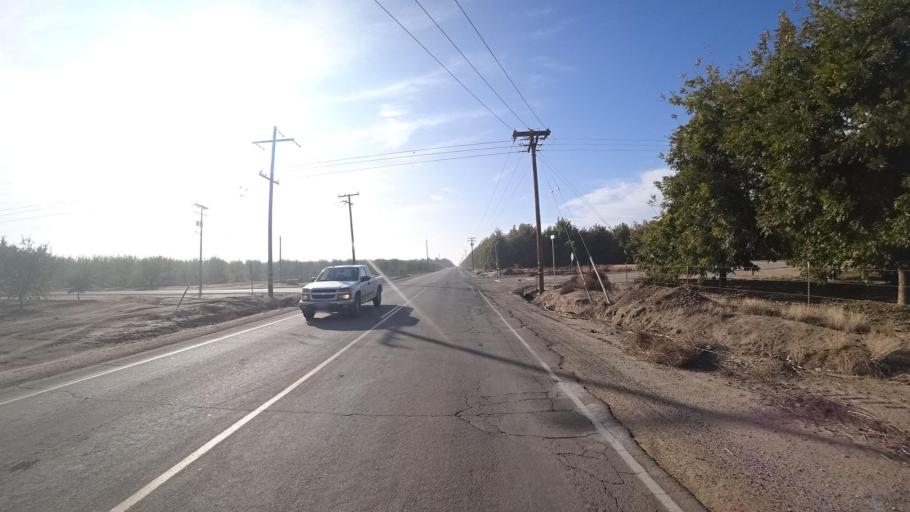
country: US
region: California
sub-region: Kern County
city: McFarland
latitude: 35.6313
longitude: -119.2045
